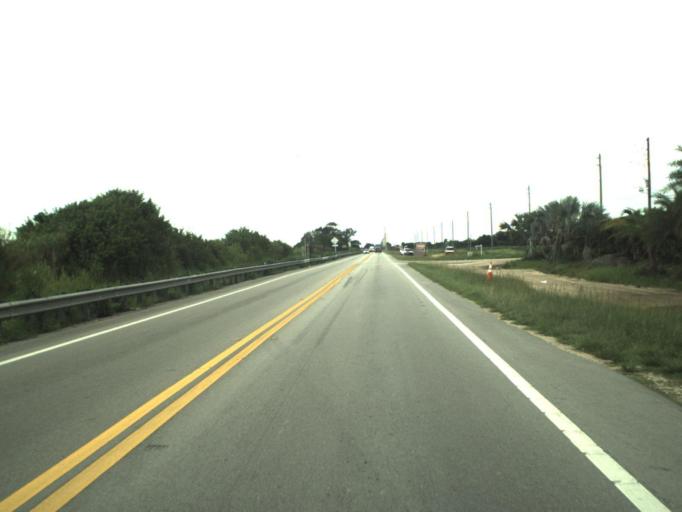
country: US
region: Florida
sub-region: Miami-Dade County
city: The Hammocks
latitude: 25.6679
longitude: -80.4811
